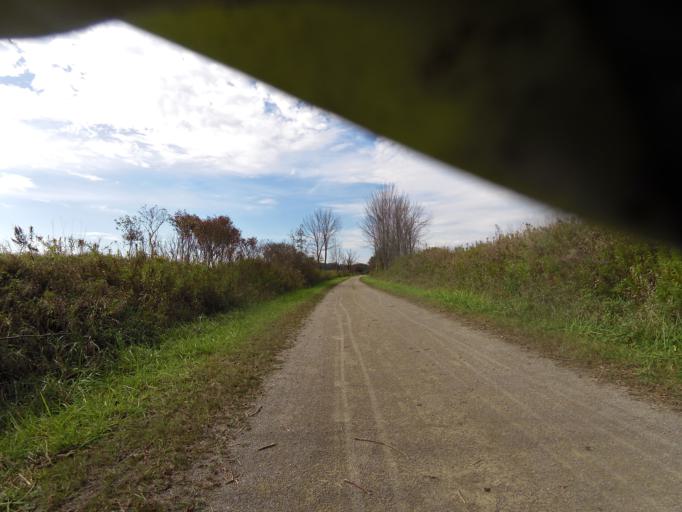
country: CA
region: Ontario
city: Ancaster
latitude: 43.1919
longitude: -80.1267
